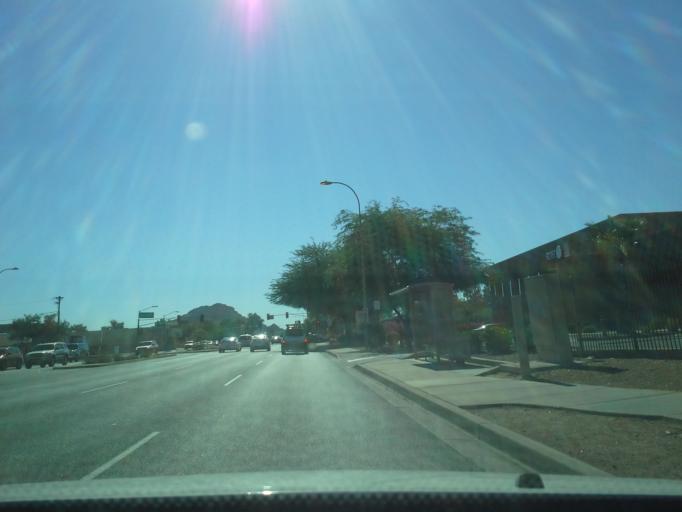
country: US
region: Arizona
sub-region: Maricopa County
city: Tempe Junction
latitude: 33.4655
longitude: -111.9832
